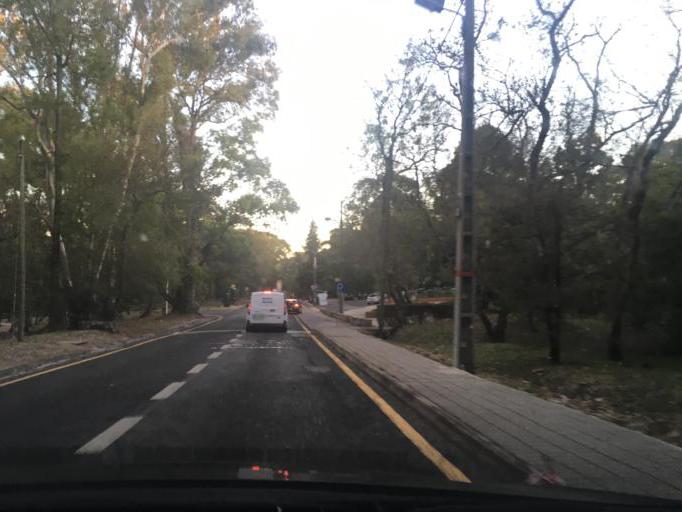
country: PT
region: Lisbon
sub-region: Oeiras
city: Alges
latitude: 38.7204
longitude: -9.1856
